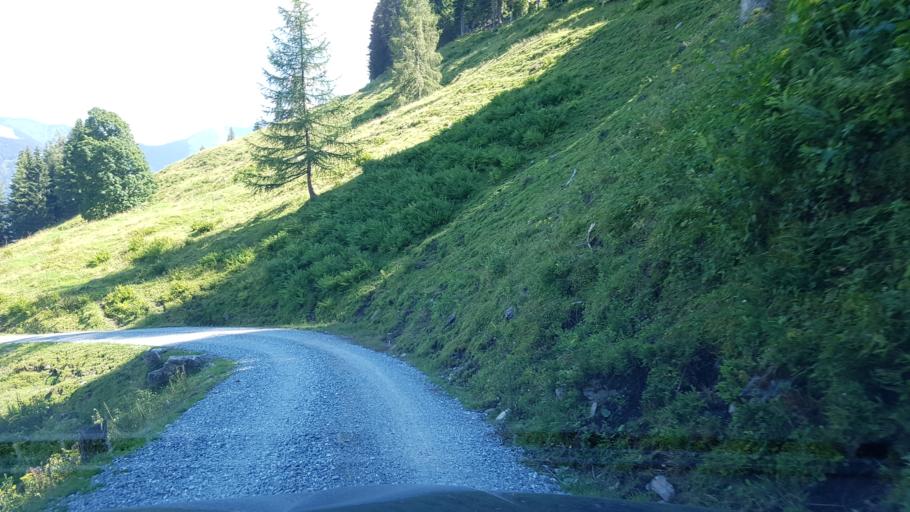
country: AT
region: Salzburg
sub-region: Politischer Bezirk Sankt Johann im Pongau
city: Dorfgastein
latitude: 47.2485
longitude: 13.0704
